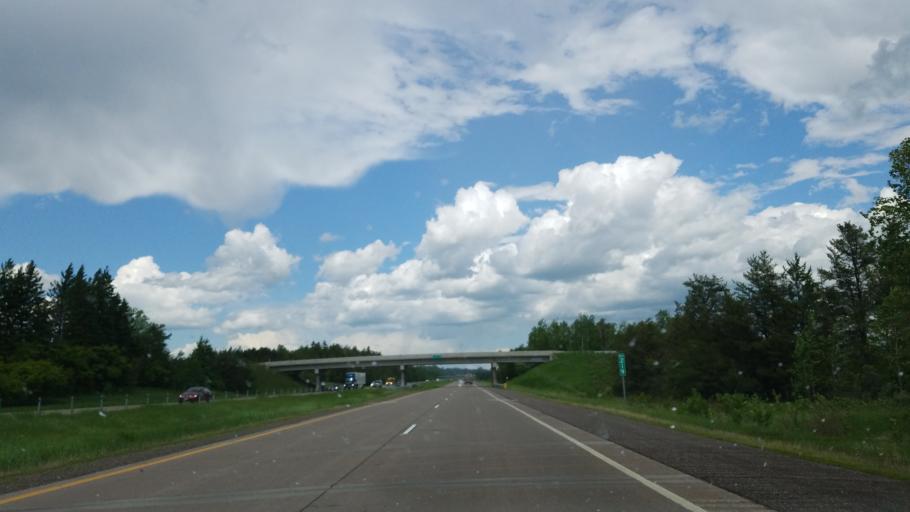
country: US
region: Minnesota
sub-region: Carlton County
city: Moose Lake
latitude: 46.4894
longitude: -92.7005
